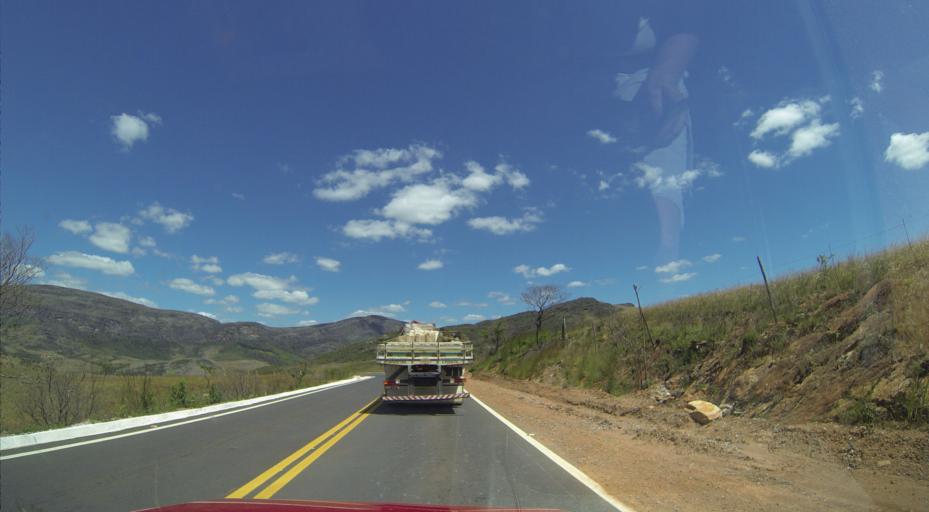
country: BR
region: Minas Gerais
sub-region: Conceicao Do Mato Dentro
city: Conceicao do Mato Dentro
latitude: -19.2878
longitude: -43.5648
